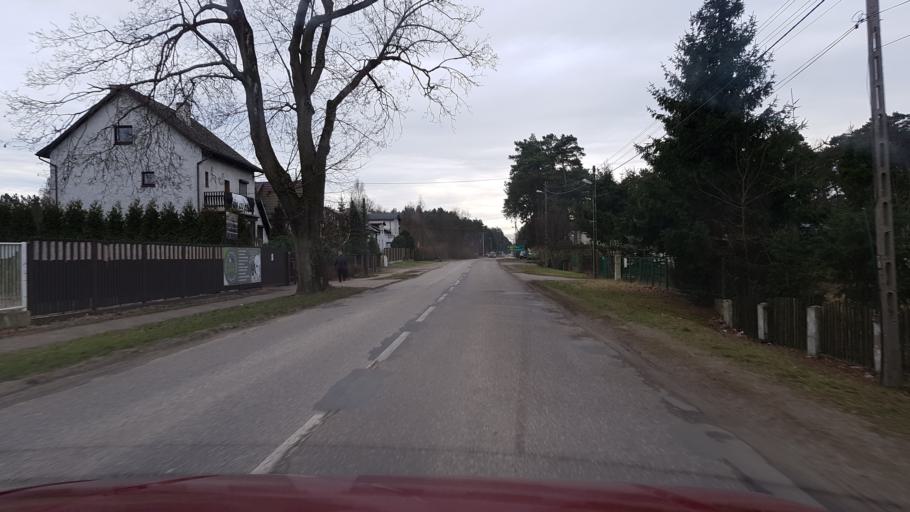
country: PL
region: West Pomeranian Voivodeship
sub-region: Powiat policki
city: Dobra
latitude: 53.5363
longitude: 14.4670
